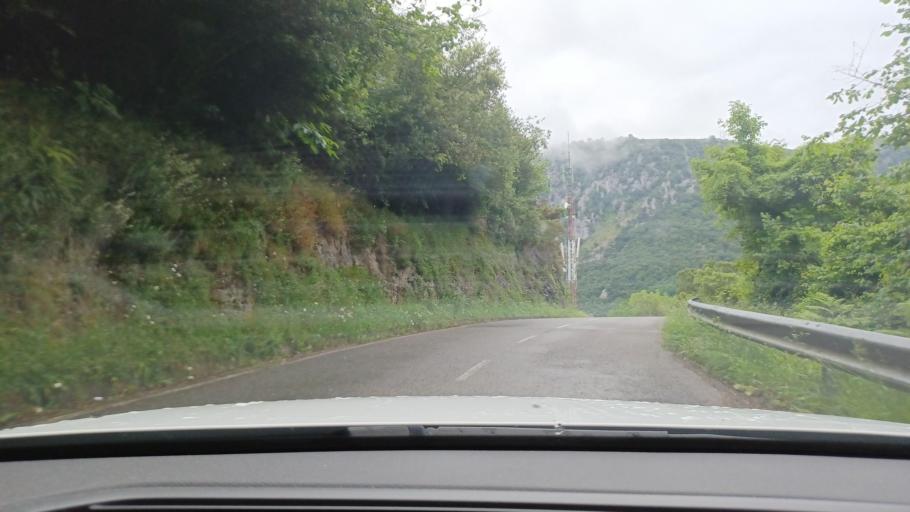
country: ES
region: Asturias
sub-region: Province of Asturias
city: Proaza
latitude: 43.2807
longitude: -5.9863
